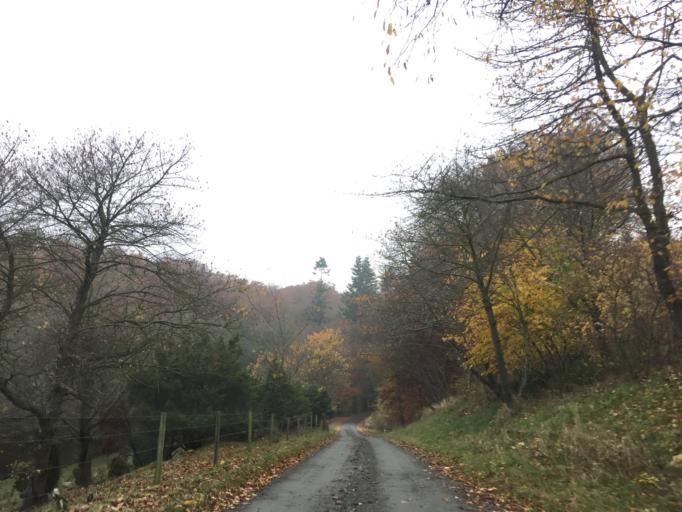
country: SE
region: Skane
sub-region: Lunds Kommun
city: Veberod
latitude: 55.6092
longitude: 13.5143
